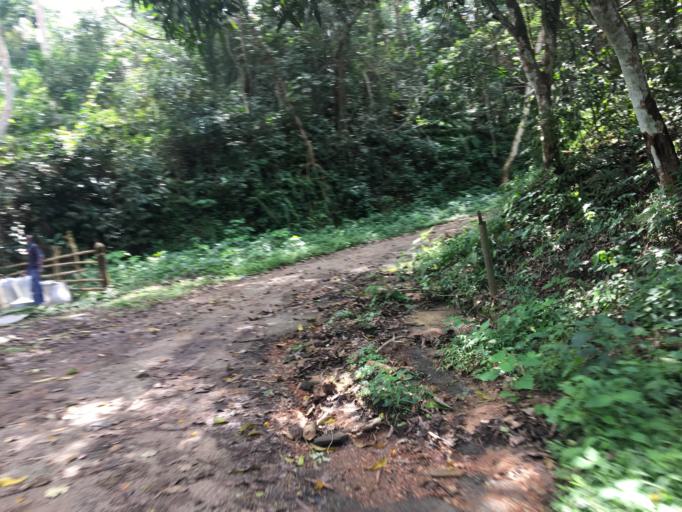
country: TG
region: Plateaux
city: Kpalime
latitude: 6.9543
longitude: 0.5846
